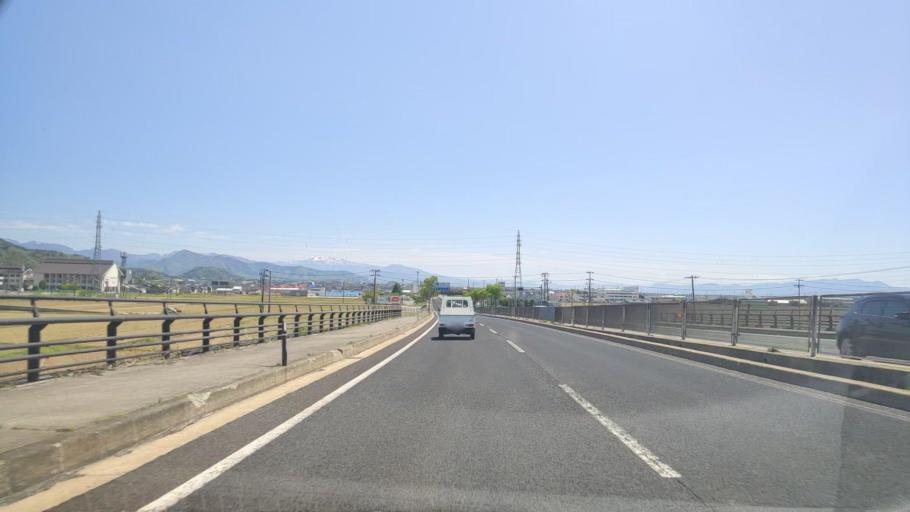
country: JP
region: Yamagata
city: Higashine
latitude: 38.4914
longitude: 140.3832
